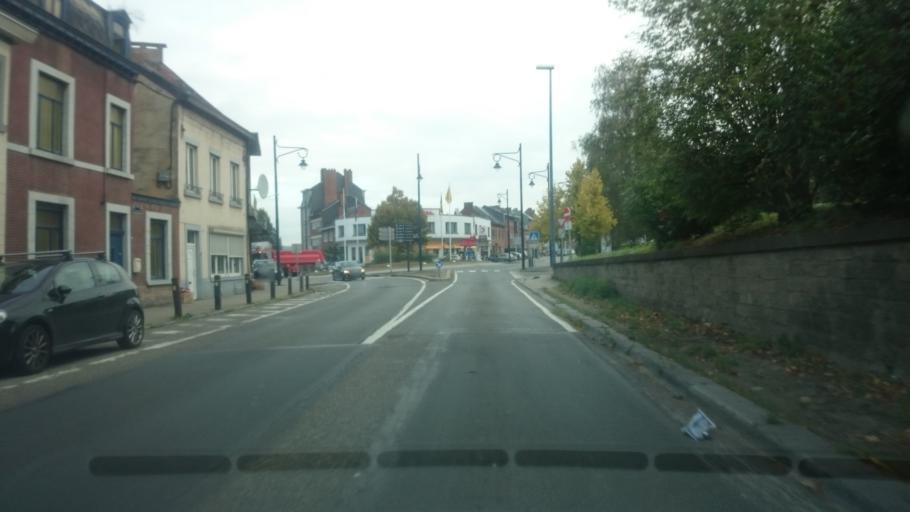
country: BE
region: Wallonia
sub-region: Province de Namur
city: Namur
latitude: 50.4606
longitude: 4.8385
